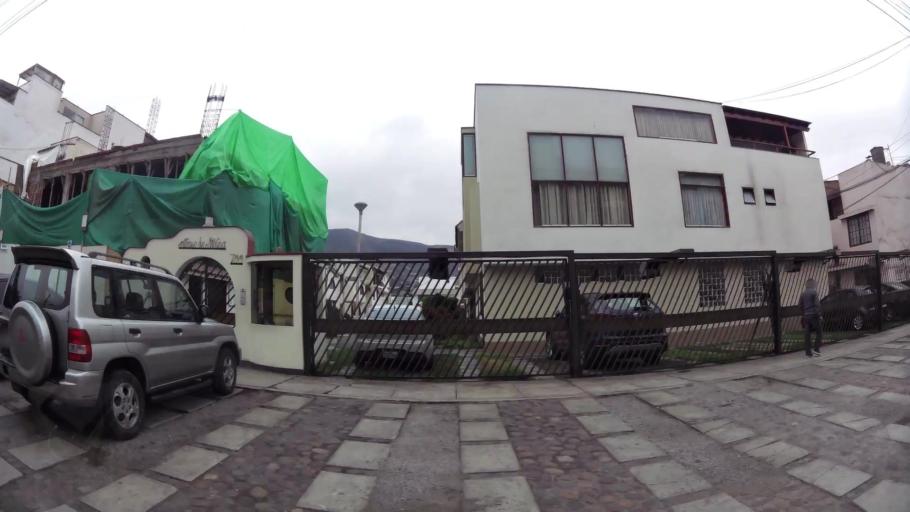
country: PE
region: Lima
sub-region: Lima
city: La Molina
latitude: -12.1114
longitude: -76.9718
